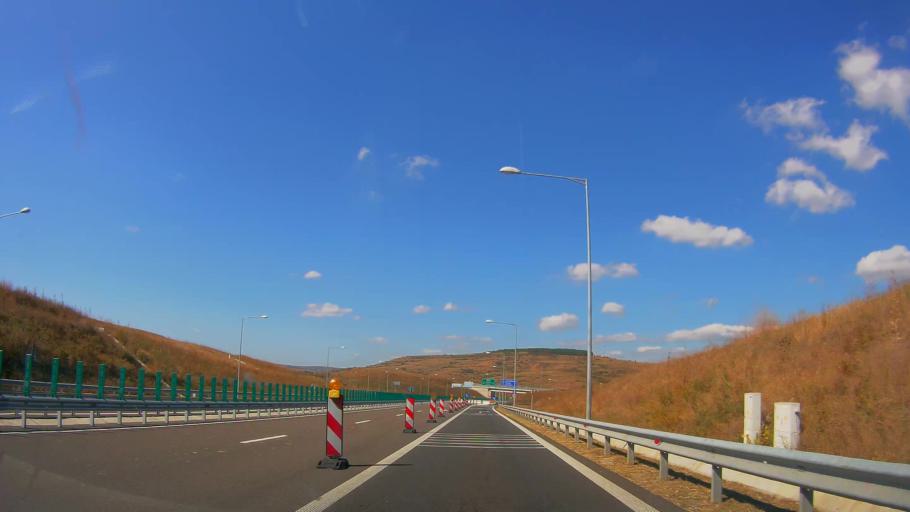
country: RO
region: Cluj
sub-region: Comuna Baciu
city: Mera
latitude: 46.8071
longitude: 23.4236
